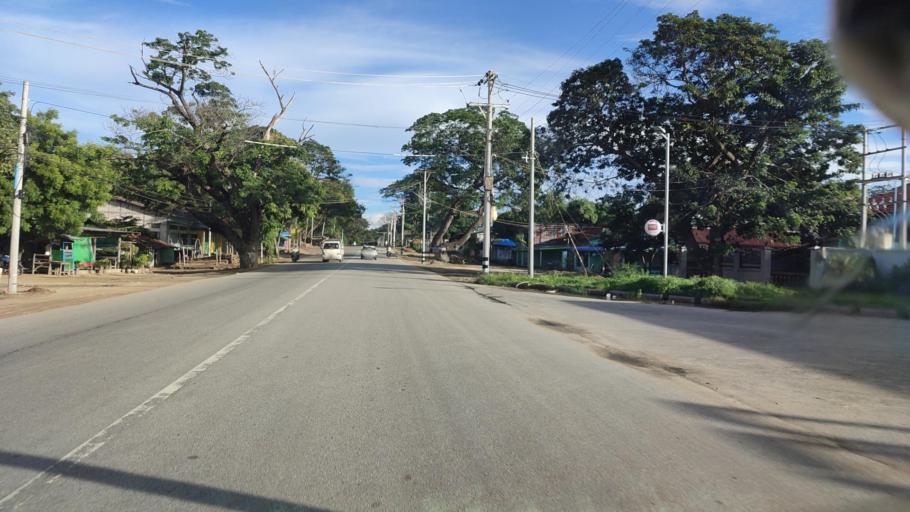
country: MM
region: Mandalay
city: Yamethin
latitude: 20.1406
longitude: 96.1961
